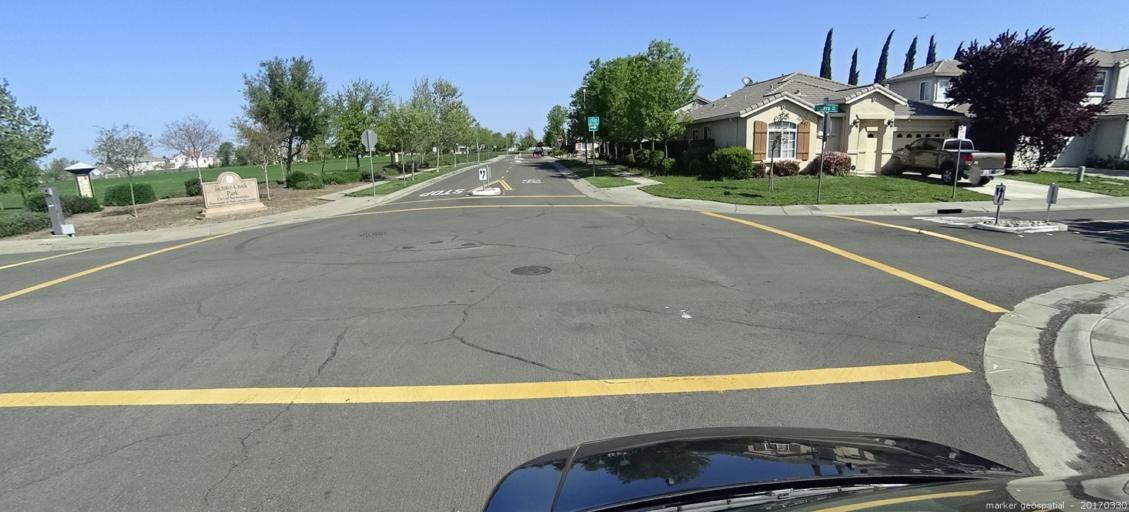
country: US
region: California
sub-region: Sacramento County
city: Laguna
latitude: 38.4436
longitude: -121.4072
